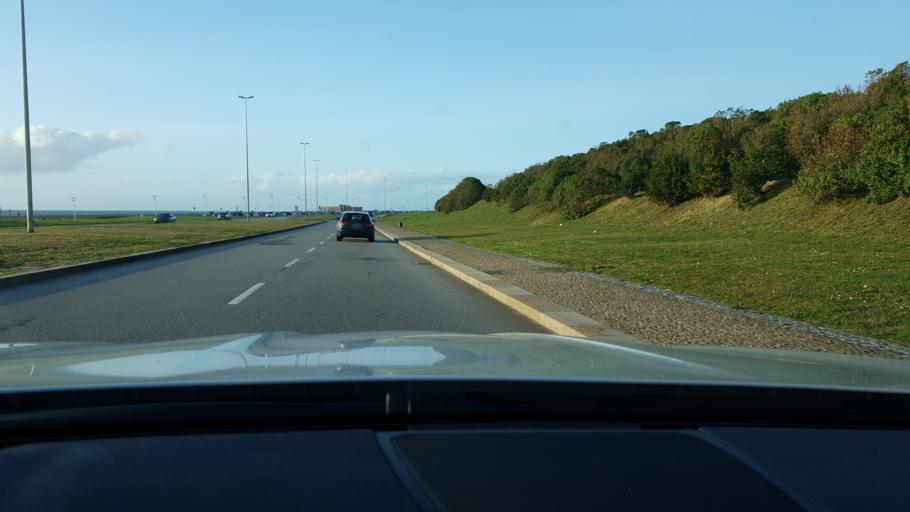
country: PT
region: Porto
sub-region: Matosinhos
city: Leca da Palmeira
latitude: 41.2042
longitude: -8.7132
